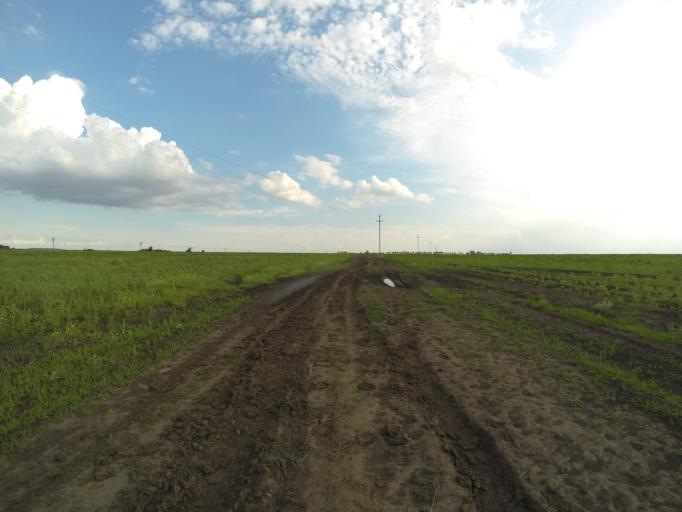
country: RO
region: Dolj
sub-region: Comuna Caloparu
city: Salcuta
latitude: 44.1520
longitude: 23.7038
